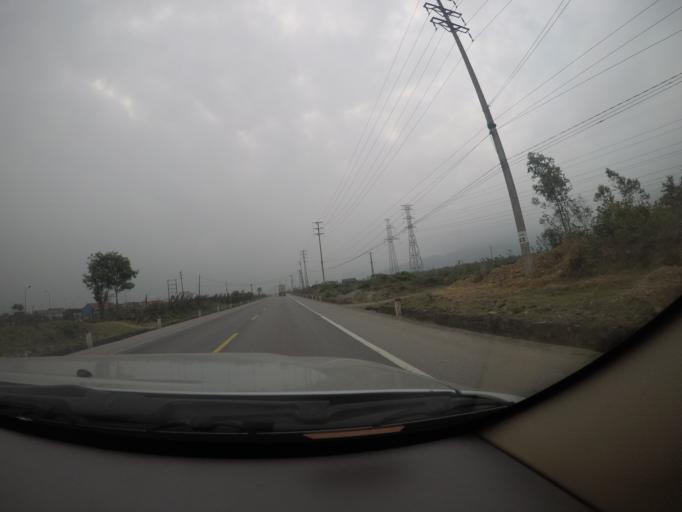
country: VN
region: Ha Tinh
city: Ky Anh
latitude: 18.0108
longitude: 106.4066
